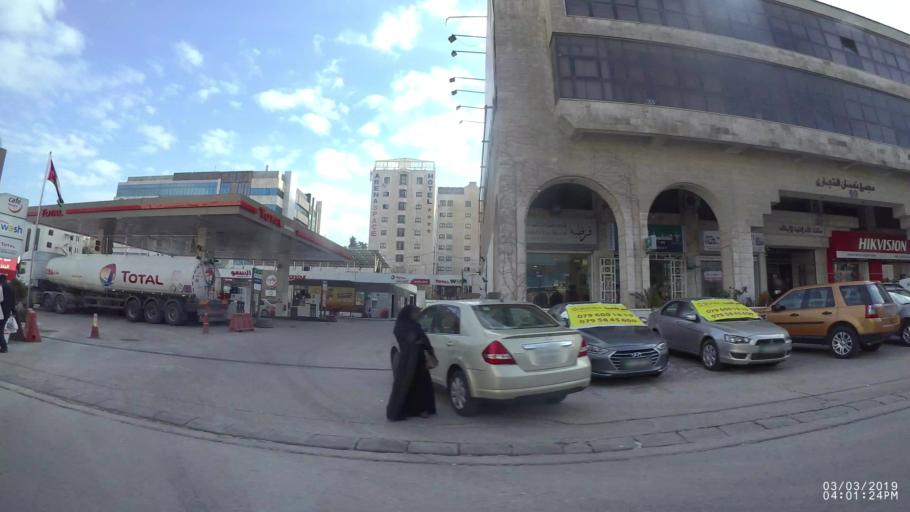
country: JO
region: Amman
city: Al Jubayhah
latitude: 31.9866
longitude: 35.8779
